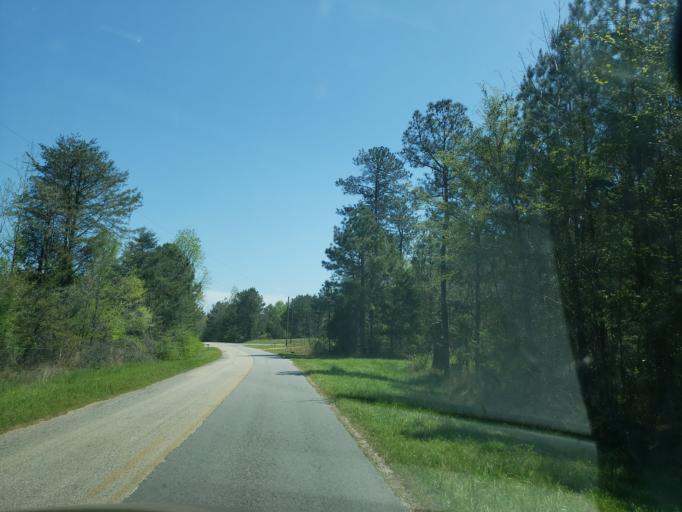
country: US
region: Alabama
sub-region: Tallapoosa County
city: Camp Hill
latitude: 32.6673
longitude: -85.7236
